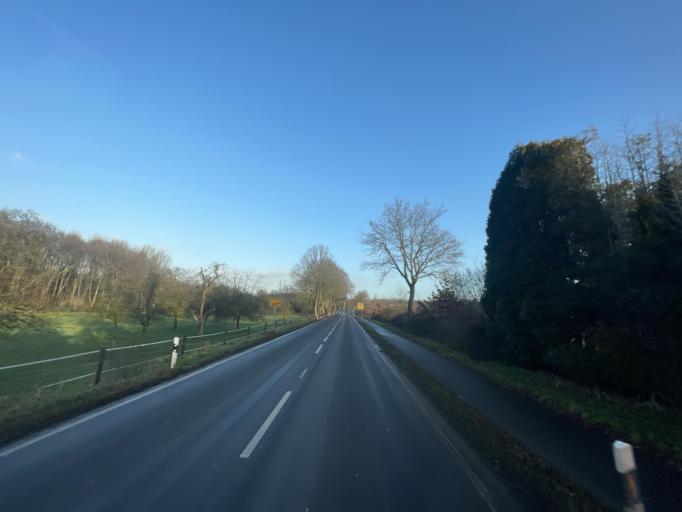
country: DE
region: North Rhine-Westphalia
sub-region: Regierungsbezirk Dusseldorf
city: Nettetal
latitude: 51.2773
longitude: 6.2727
